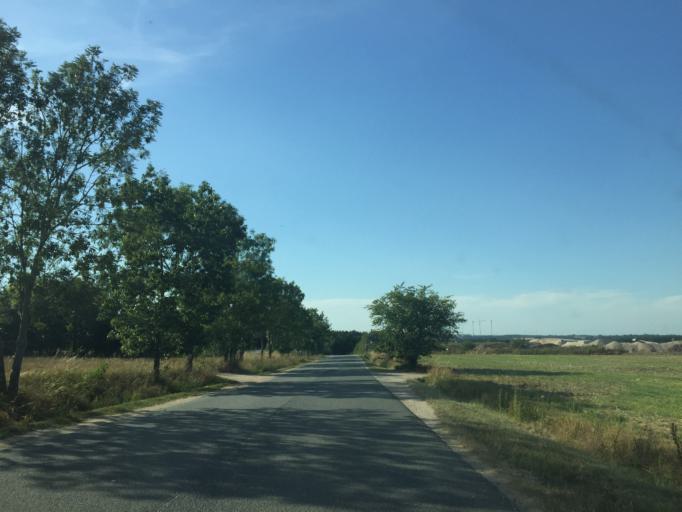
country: DE
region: Thuringia
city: Heyersdorf
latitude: 50.8561
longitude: 12.3434
